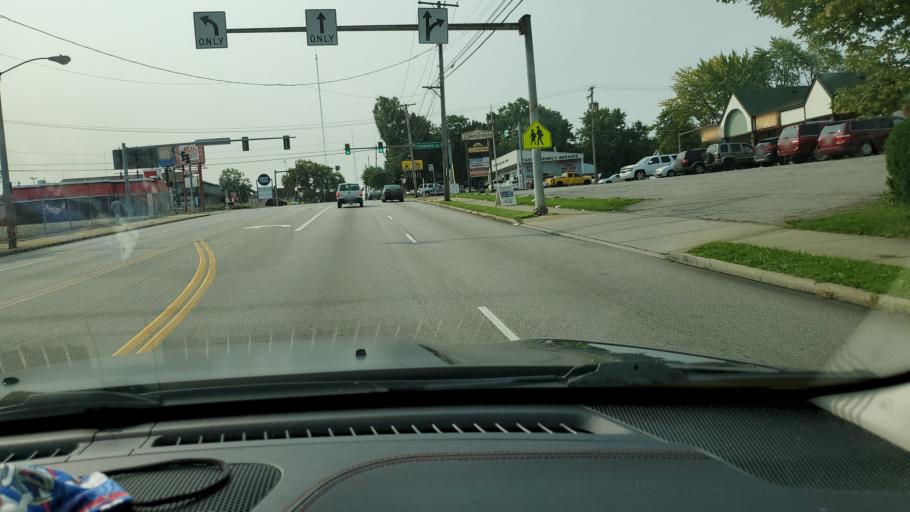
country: US
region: Ohio
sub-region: Mahoning County
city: Youngstown
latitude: 41.0734
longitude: -80.6463
